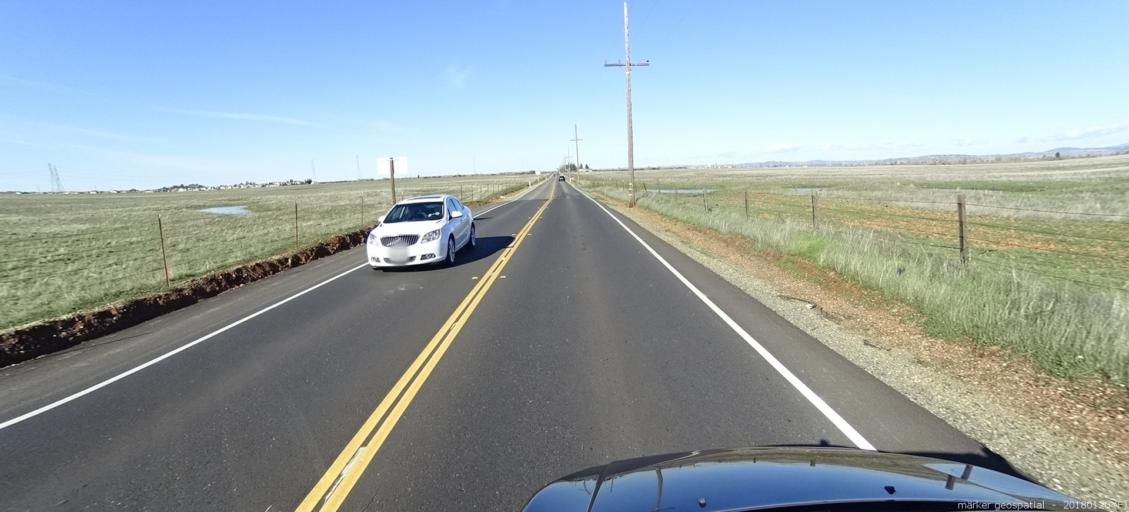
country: US
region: California
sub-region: Sacramento County
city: Gold River
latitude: 38.5608
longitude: -121.1872
